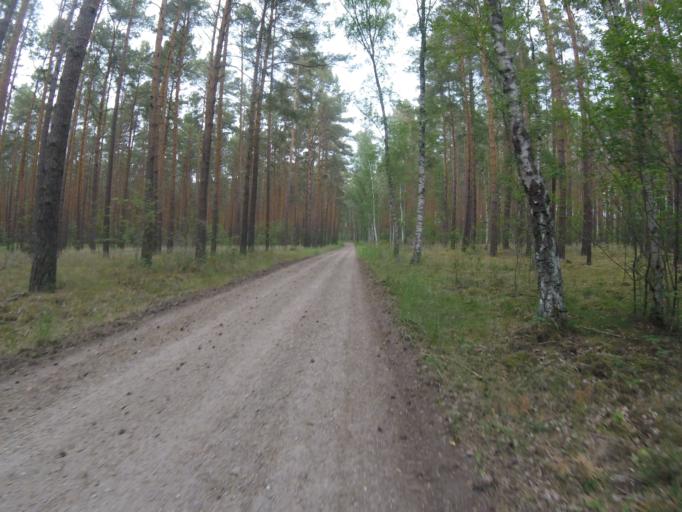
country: DE
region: Brandenburg
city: Gross Koris
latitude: 52.2038
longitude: 13.6984
